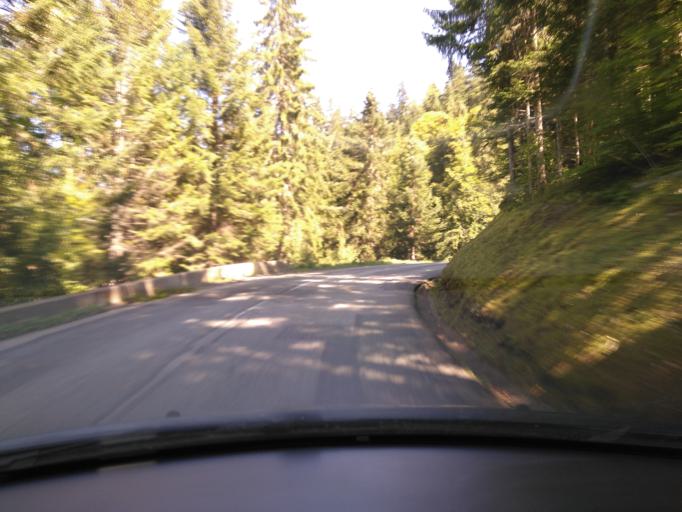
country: FR
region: Rhone-Alpes
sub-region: Departement de la Haute-Savoie
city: Praz-sur-Arly
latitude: 45.8016
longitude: 6.5006
